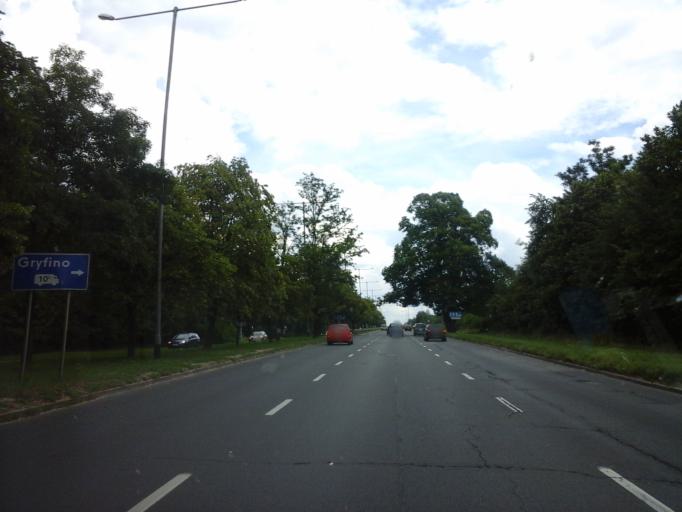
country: PL
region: West Pomeranian Voivodeship
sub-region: Powiat gryfinski
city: Stare Czarnowo
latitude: 53.3756
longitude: 14.6962
